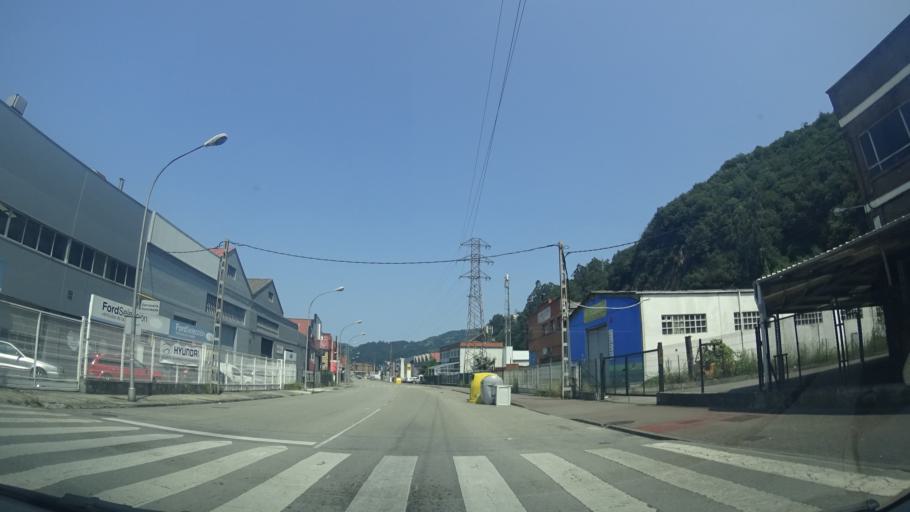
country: ES
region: Asturias
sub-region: Province of Asturias
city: Mieres
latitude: 43.2318
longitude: -5.7799
